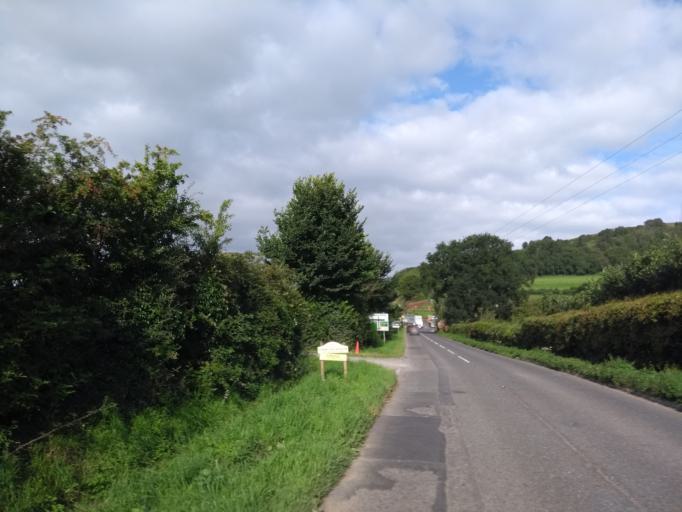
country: GB
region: England
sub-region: Somerset
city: Axbridge
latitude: 51.2893
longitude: -2.8313
